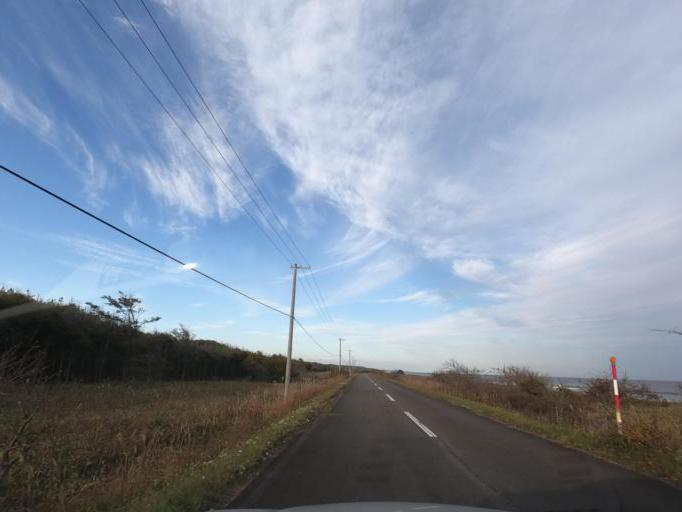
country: JP
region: Hokkaido
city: Obihiro
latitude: 42.5391
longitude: 143.4894
